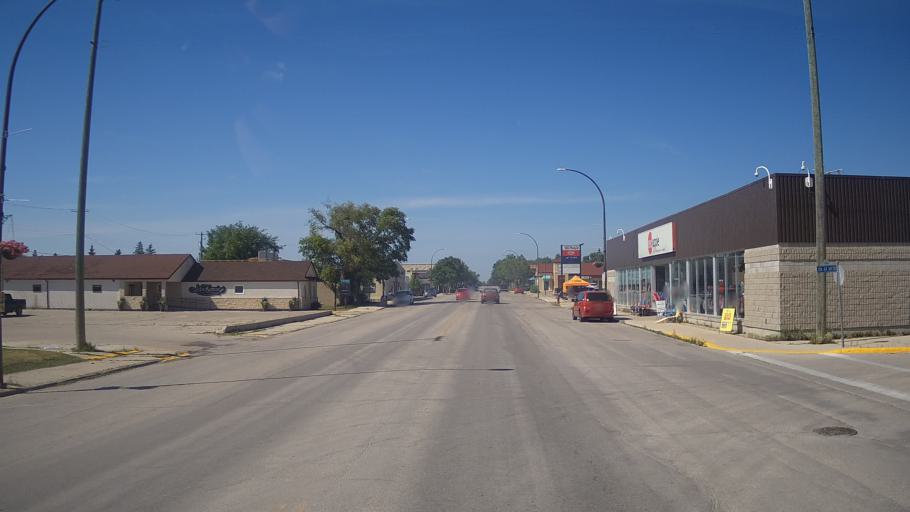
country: CA
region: Manitoba
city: Stonewall
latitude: 50.1318
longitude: -97.3265
